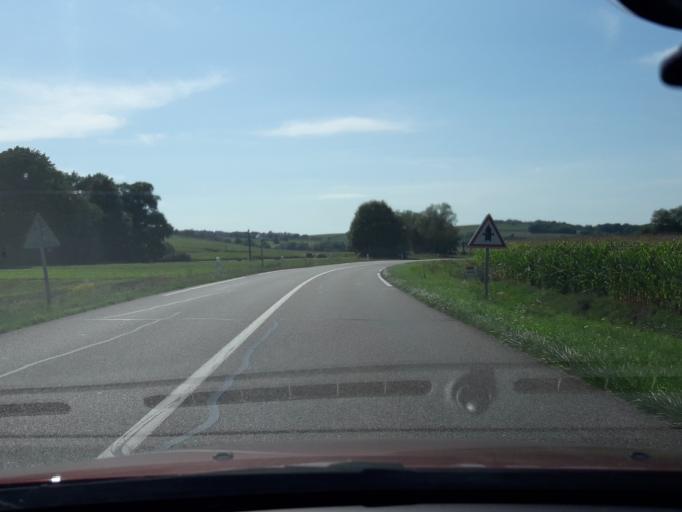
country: FR
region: Alsace
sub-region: Departement du Bas-Rhin
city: Dauendorf
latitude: 48.8403
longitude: 7.6707
